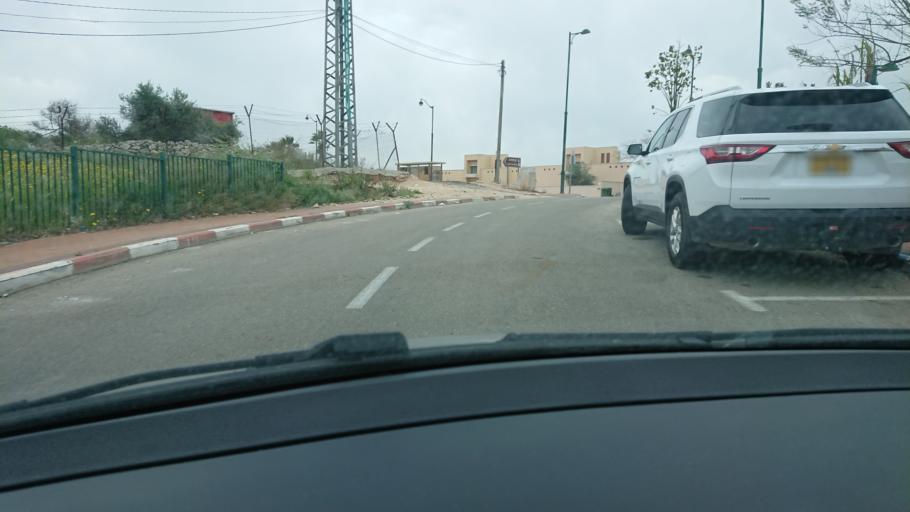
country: PS
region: West Bank
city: Rafat
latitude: 32.0653
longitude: 35.0566
